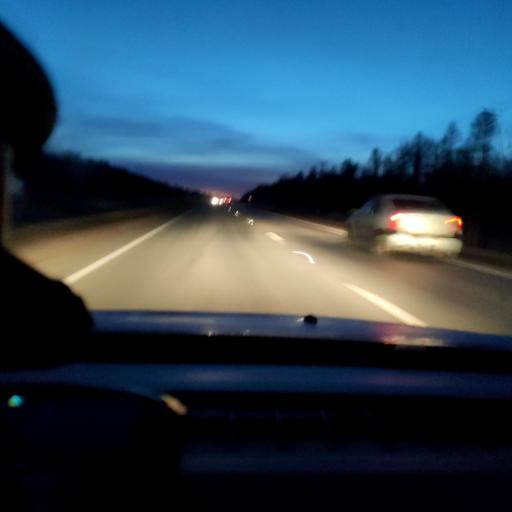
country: RU
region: Samara
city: Chapayevsk
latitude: 52.9962
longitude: 49.7961
